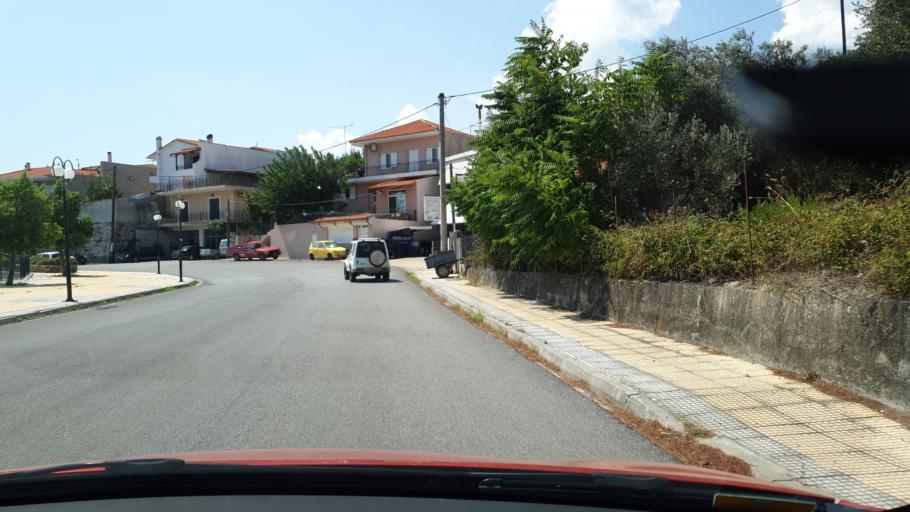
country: GR
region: Central Greece
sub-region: Nomos Evvoias
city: Oxilithos
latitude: 38.5788
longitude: 24.0603
